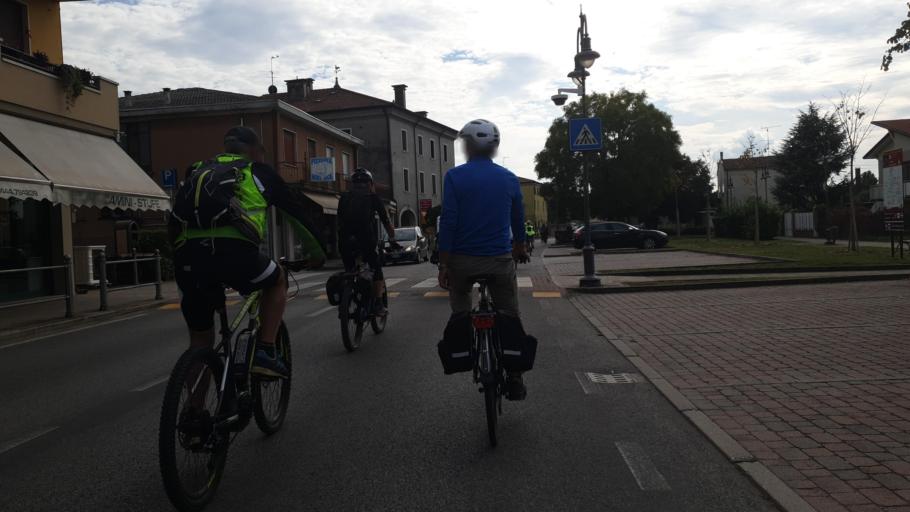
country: IT
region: Veneto
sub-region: Provincia di Vicenza
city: Poiana Maggiore
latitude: 45.2891
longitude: 11.5007
